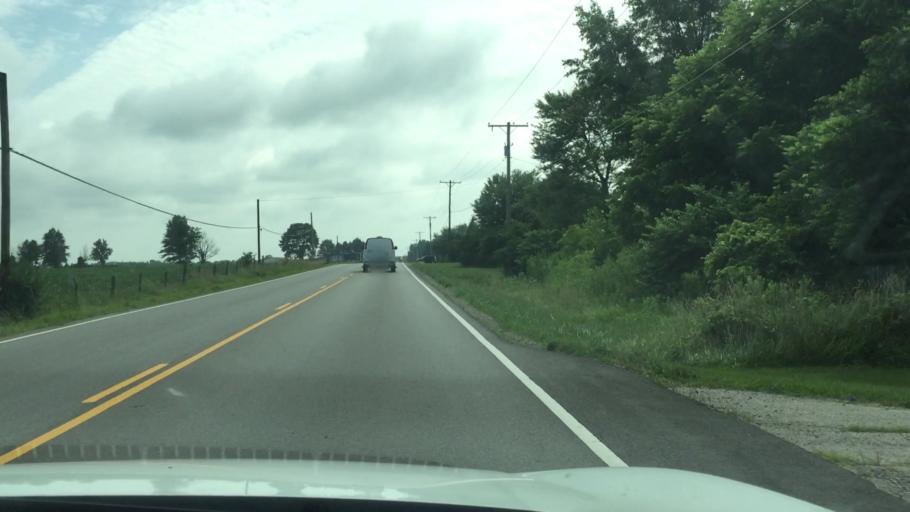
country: US
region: Ohio
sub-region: Union County
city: Marysville
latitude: 40.1915
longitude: -83.4201
